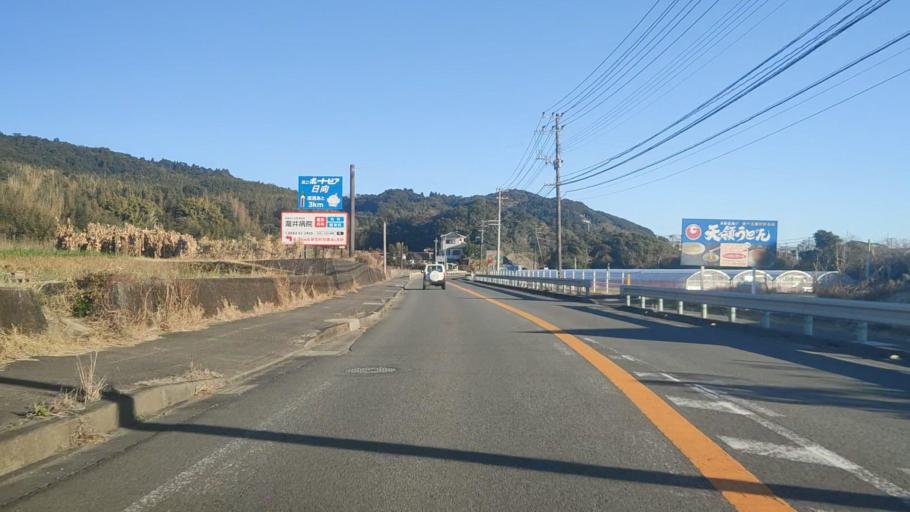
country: JP
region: Miyazaki
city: Nobeoka
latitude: 32.3628
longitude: 131.6230
